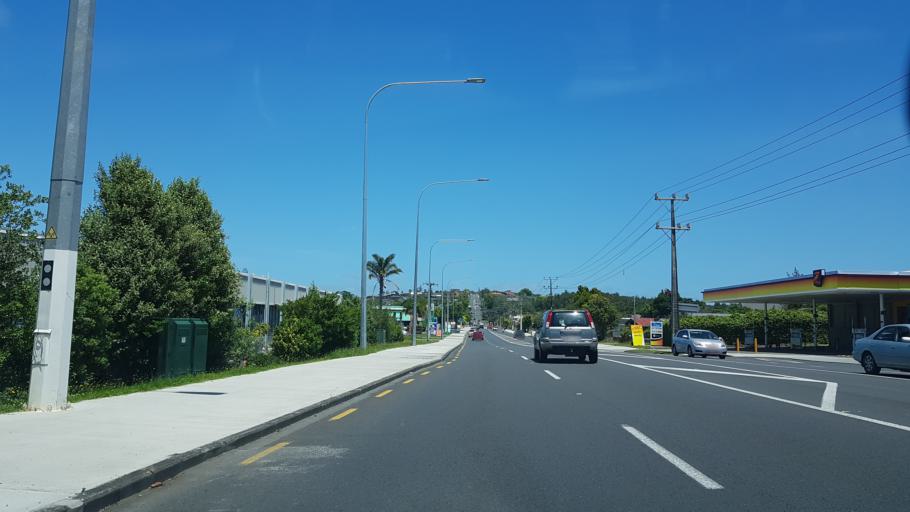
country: NZ
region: Auckland
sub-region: Auckland
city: North Shore
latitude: -36.7922
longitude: 174.7479
